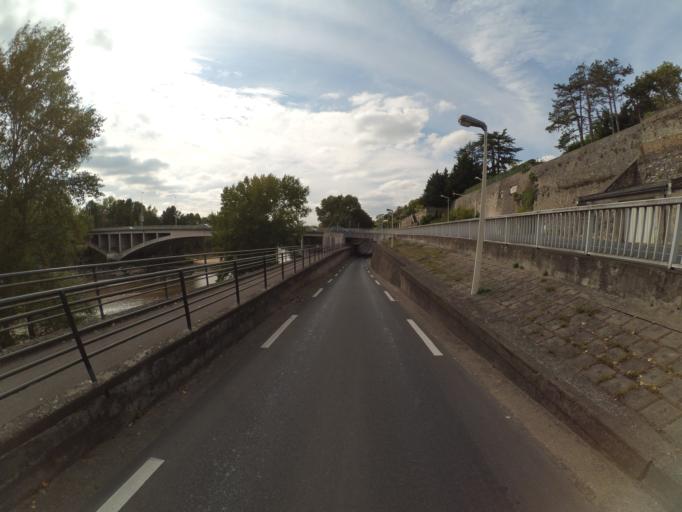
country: FR
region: Centre
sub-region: Departement d'Indre-et-Loire
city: Saint-Cyr-sur-Loire
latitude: 47.4003
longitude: 0.6771
